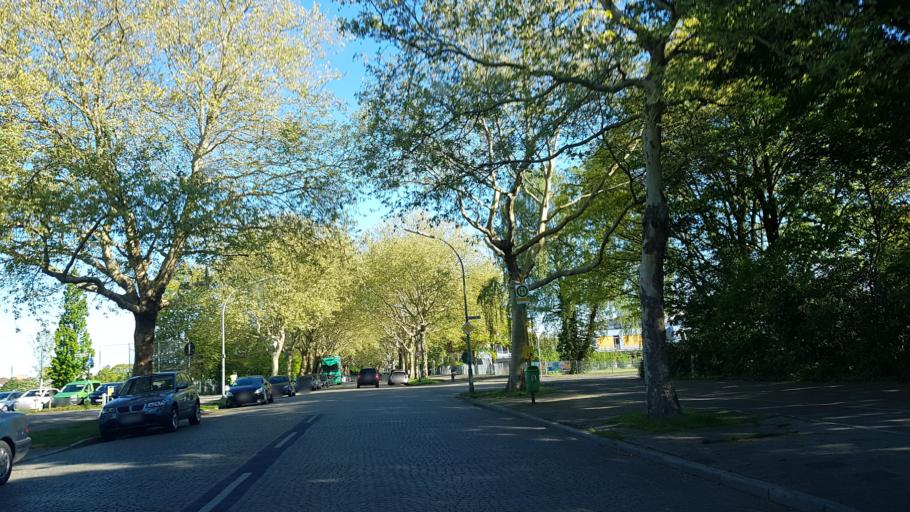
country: DE
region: Bremen
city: Bremerhaven
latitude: 53.5573
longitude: 8.5745
